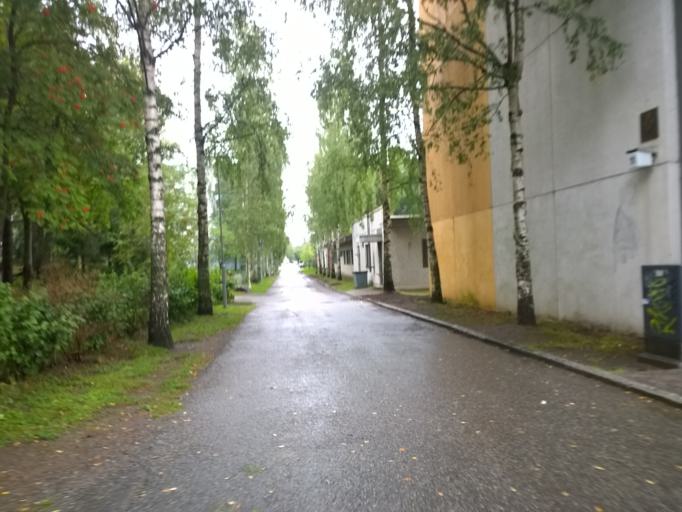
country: FI
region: Pirkanmaa
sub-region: Tampere
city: Tampere
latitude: 61.4448
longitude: 23.8438
